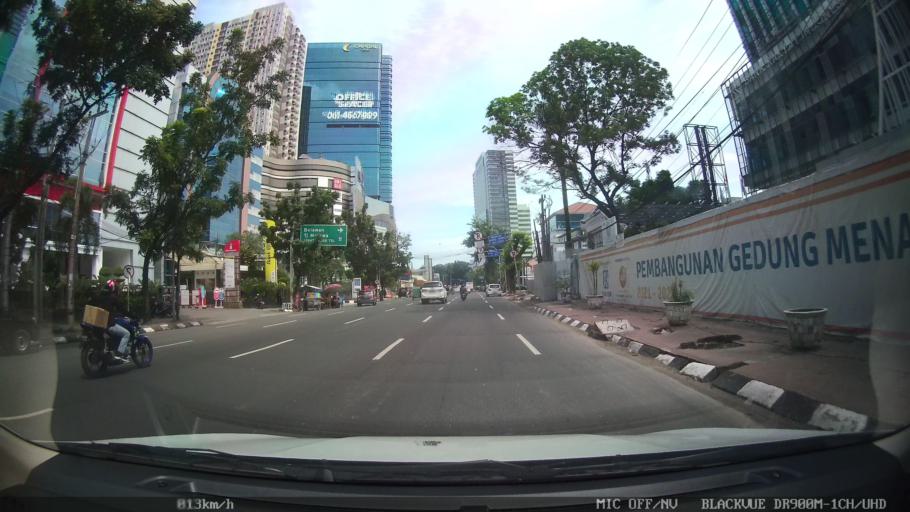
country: ID
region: North Sumatra
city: Medan
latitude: 3.5932
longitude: 98.6765
